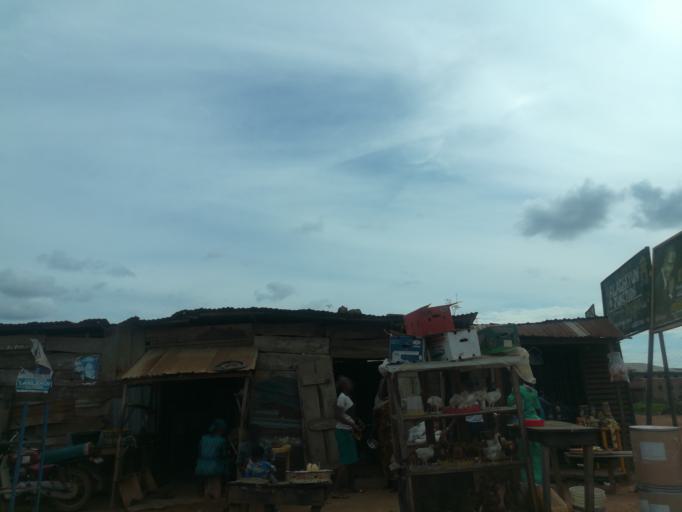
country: NG
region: Oyo
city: Ibadan
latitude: 7.3768
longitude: 3.9611
